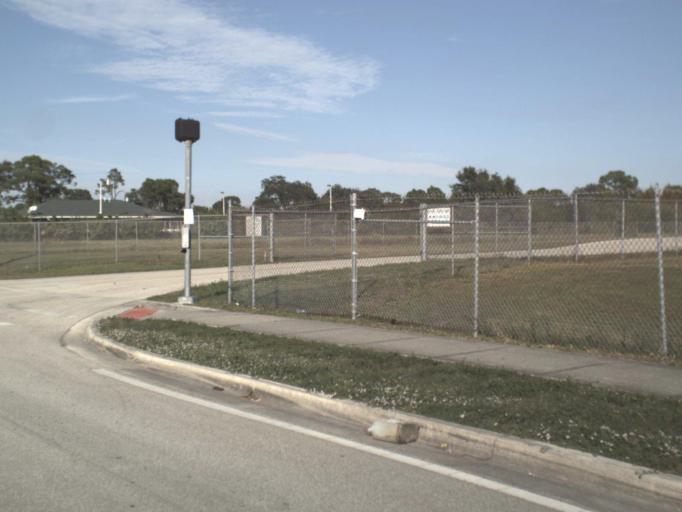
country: US
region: Florida
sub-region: Brevard County
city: June Park
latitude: 28.0632
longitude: -80.6707
